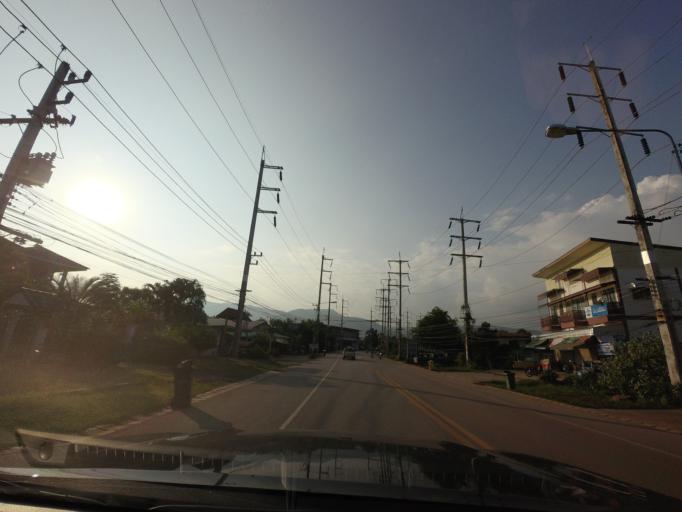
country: TH
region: Loei
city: Dan Sai
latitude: 17.2728
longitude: 101.1425
